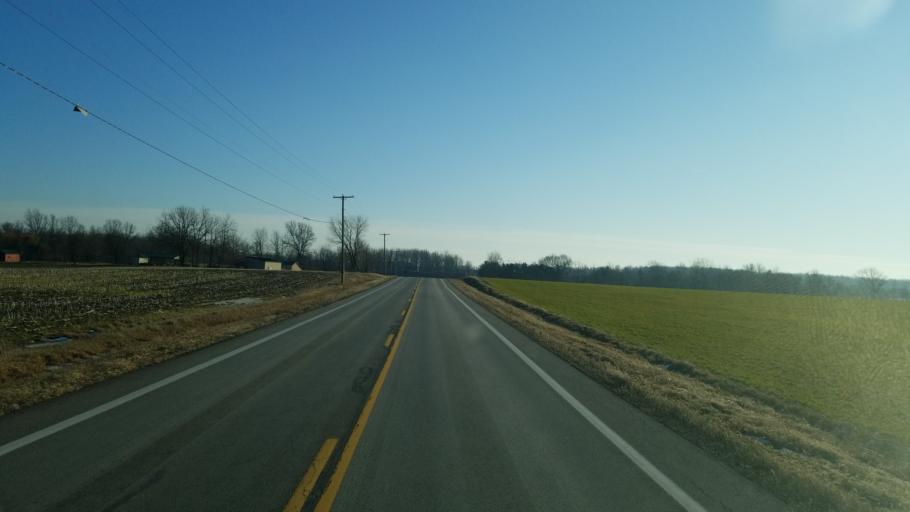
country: US
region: Ohio
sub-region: Seneca County
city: Tiffin
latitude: 41.0292
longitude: -83.0163
